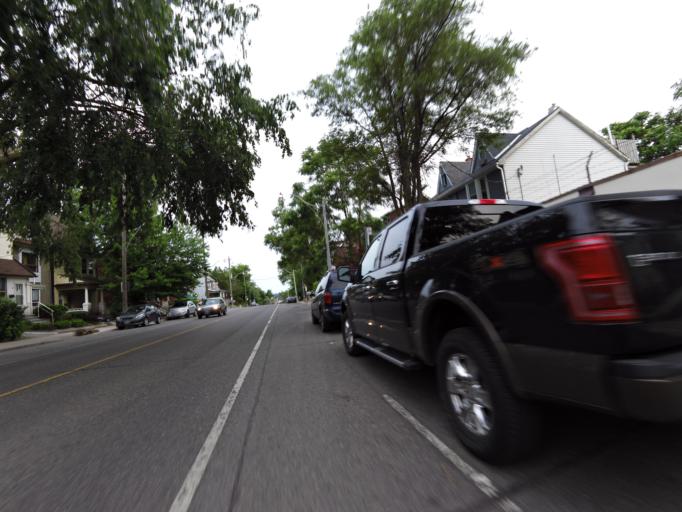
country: CA
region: Ontario
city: Toronto
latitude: 43.6758
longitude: -79.3385
